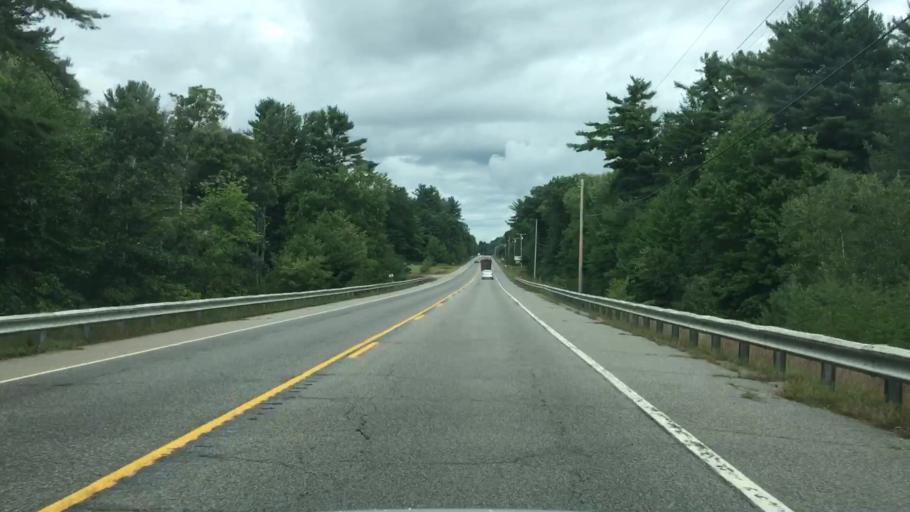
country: US
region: Maine
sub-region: York County
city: South Sanford
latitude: 43.3865
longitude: -70.7400
